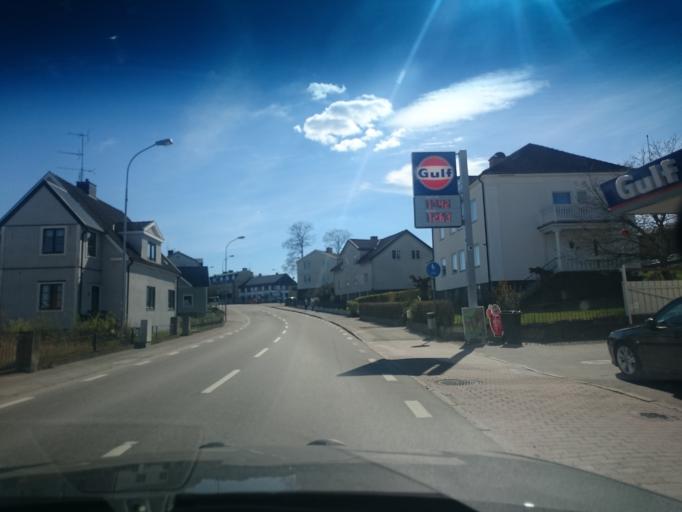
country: SE
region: Kalmar
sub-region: Hultsfreds Kommun
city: Virserum
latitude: 57.3210
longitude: 15.5818
